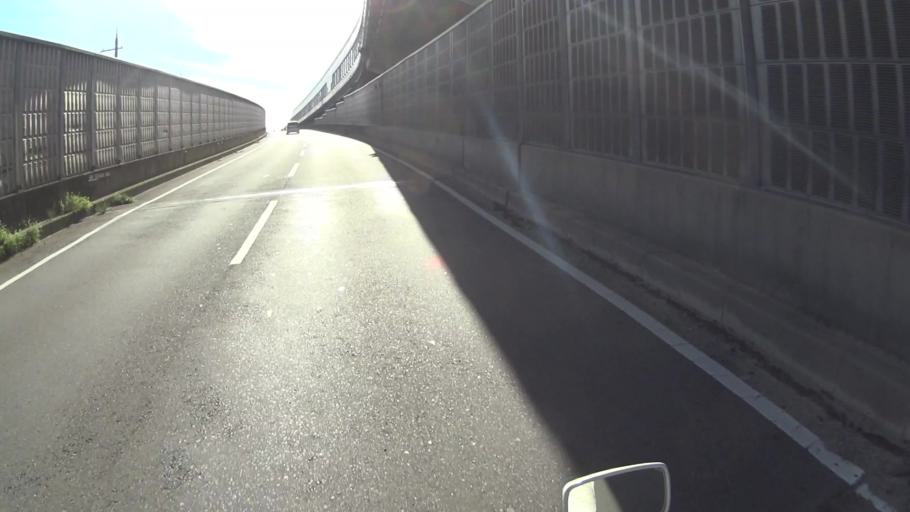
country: JP
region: Kyoto
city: Uji
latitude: 34.9058
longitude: 135.7766
